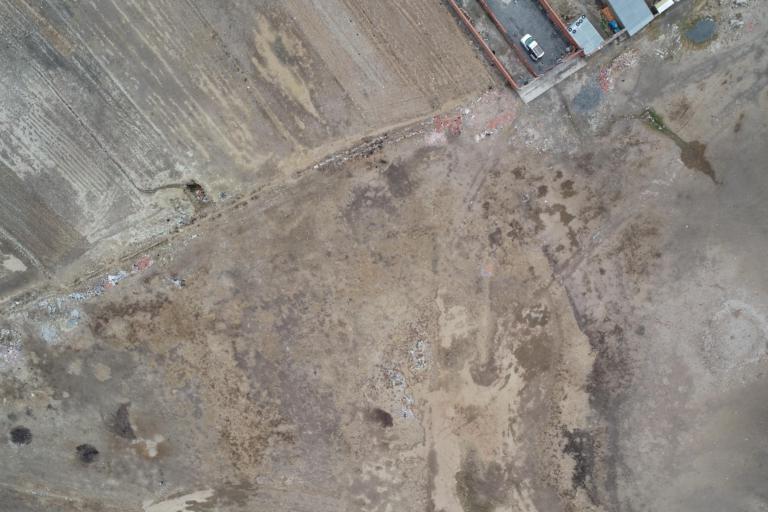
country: BO
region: La Paz
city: Achacachi
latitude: -16.0542
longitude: -68.6887
